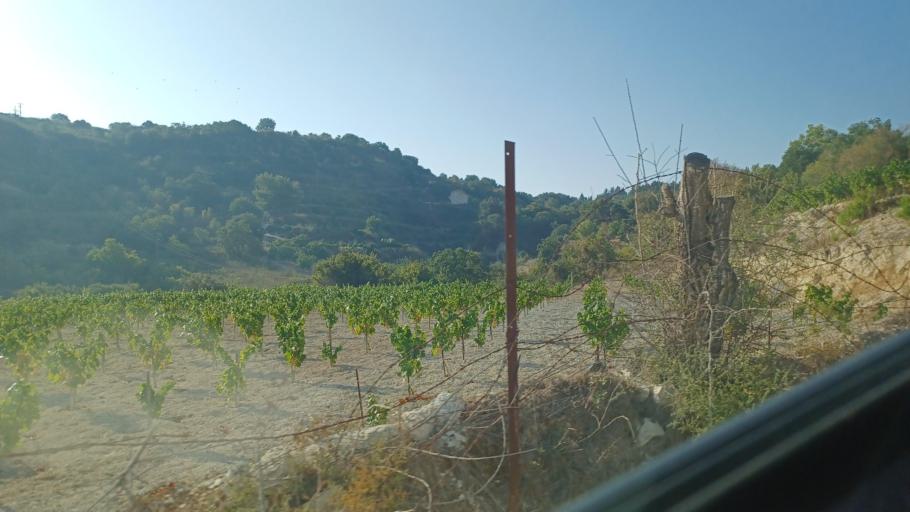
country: CY
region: Pafos
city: Mesogi
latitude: 34.8411
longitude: 32.4797
